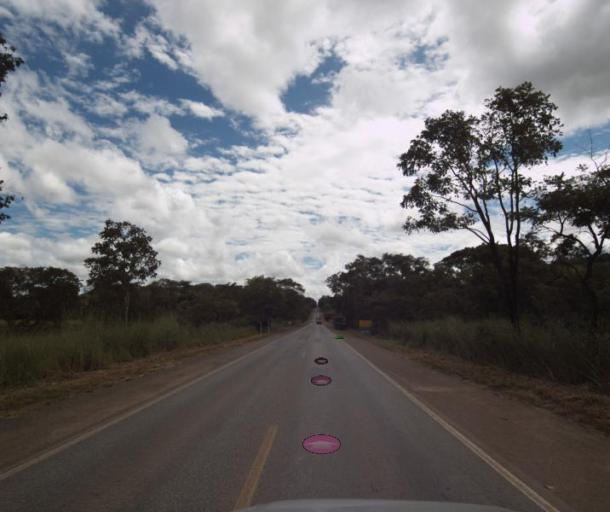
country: BR
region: Goias
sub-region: Uruacu
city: Uruacu
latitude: -14.4180
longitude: -49.1572
